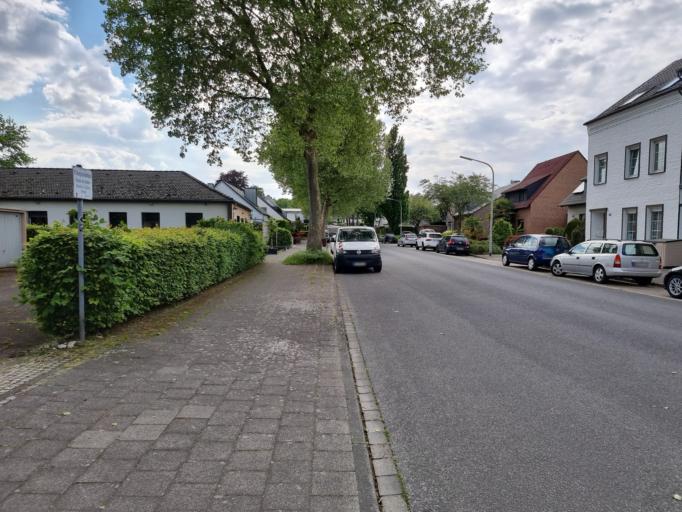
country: DE
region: North Rhine-Westphalia
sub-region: Regierungsbezirk Dusseldorf
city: Monchengladbach
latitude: 51.2133
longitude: 6.4463
